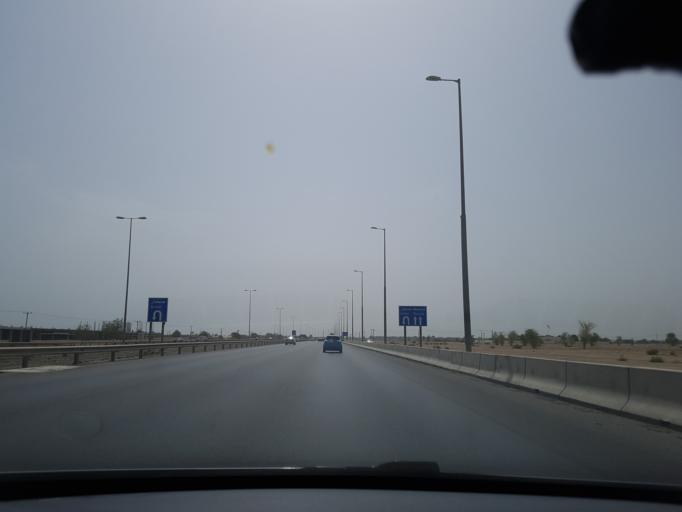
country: OM
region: Al Batinah
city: As Suwayq
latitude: 23.8216
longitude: 57.4331
